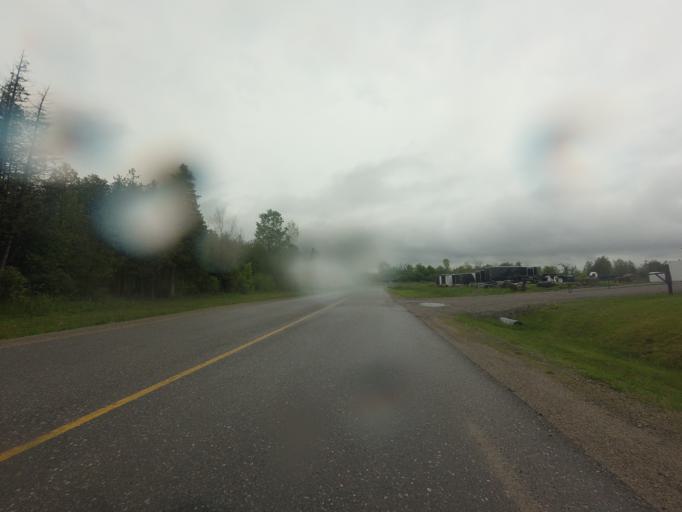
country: CA
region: Ontario
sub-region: Lanark County
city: Smiths Falls
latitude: 44.8715
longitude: -76.0424
